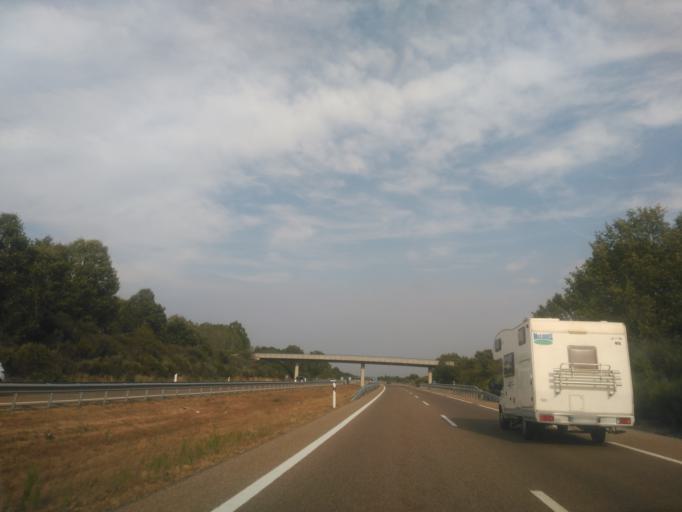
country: ES
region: Castille and Leon
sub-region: Provincia de Zamora
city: Asturianos
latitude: 42.0438
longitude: -6.4857
